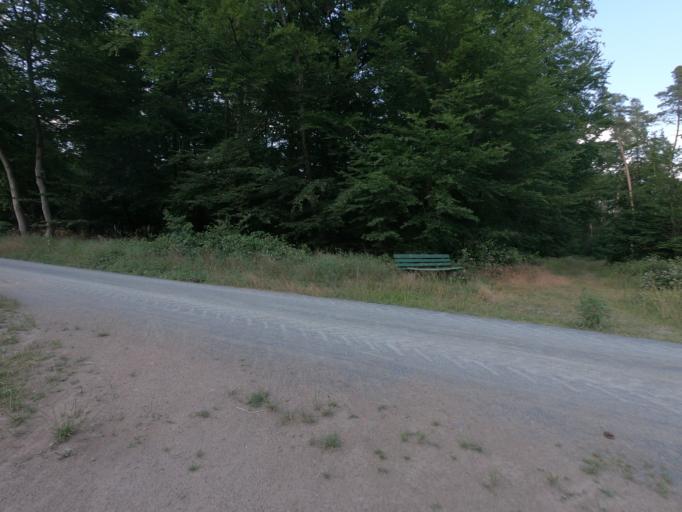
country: DE
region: Hesse
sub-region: Regierungsbezirk Darmstadt
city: Nauheim
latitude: 49.9801
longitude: 8.4703
